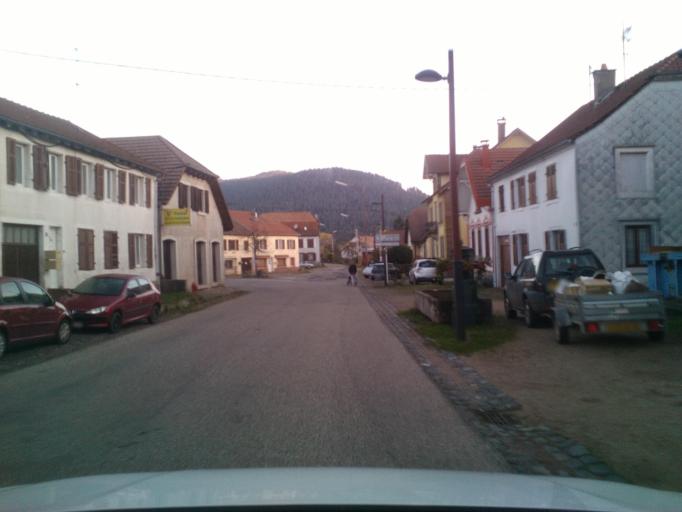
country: FR
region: Lorraine
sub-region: Departement des Vosges
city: Ban-de-Laveline
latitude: 48.3493
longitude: 7.1064
